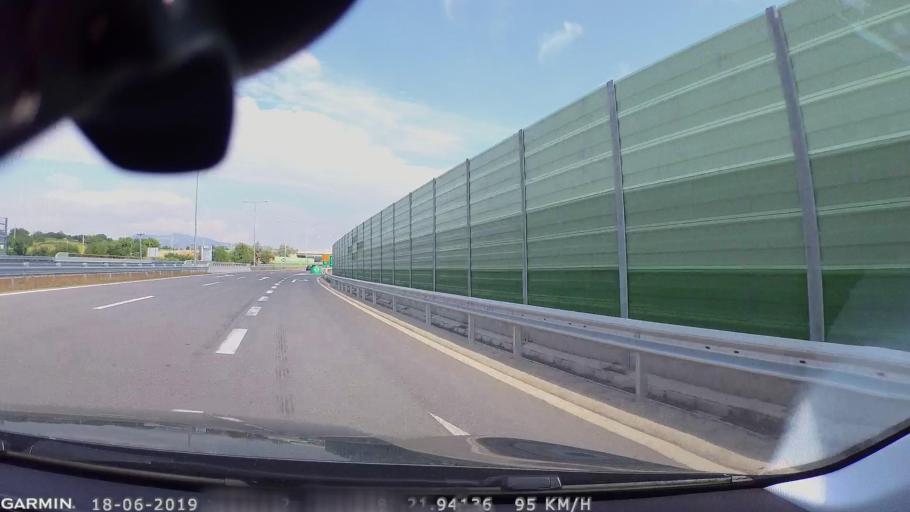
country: MK
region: Sveti Nikole
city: Sveti Nikole
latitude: 41.8757
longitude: 21.9415
